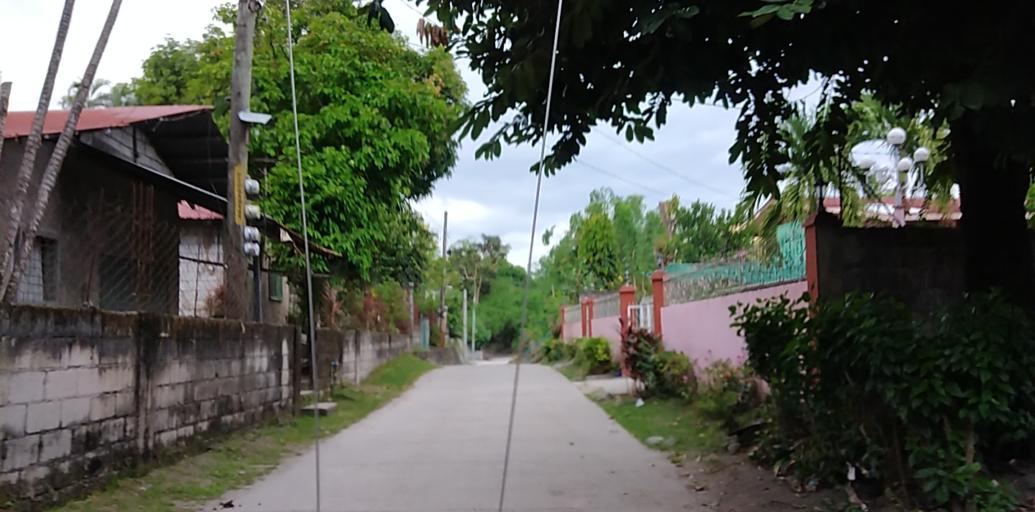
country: PH
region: Central Luzon
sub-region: Province of Pampanga
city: Pulung Santol
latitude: 15.0432
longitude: 120.5632
